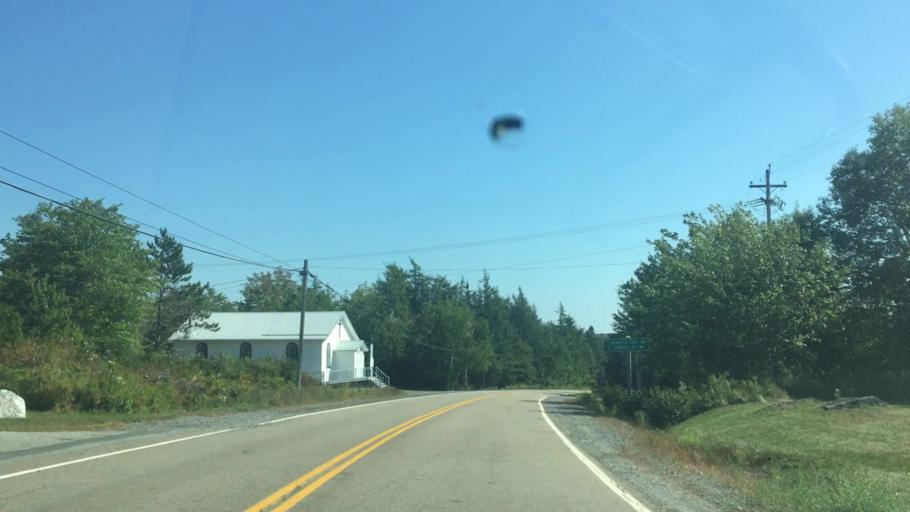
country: CA
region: Nova Scotia
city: Antigonish
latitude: 45.1447
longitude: -61.9886
